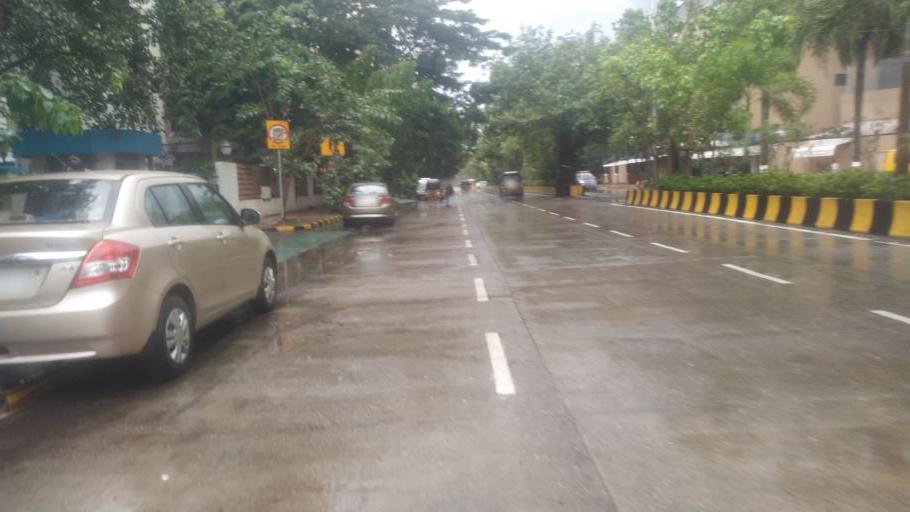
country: IN
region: Maharashtra
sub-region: Mumbai Suburban
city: Mumbai
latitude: 19.0672
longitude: 72.8698
